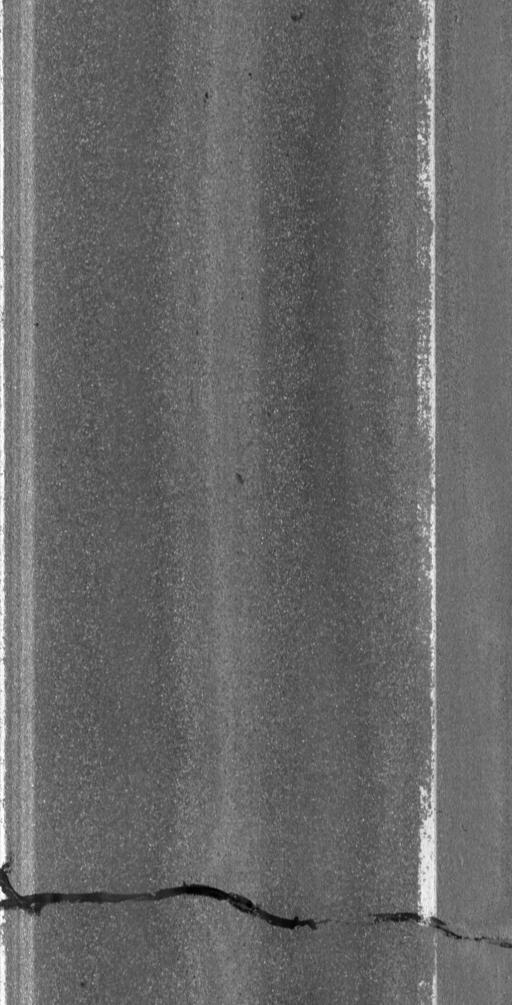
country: US
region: Vermont
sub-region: Washington County
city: Northfield
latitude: 44.1716
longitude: -72.8322
